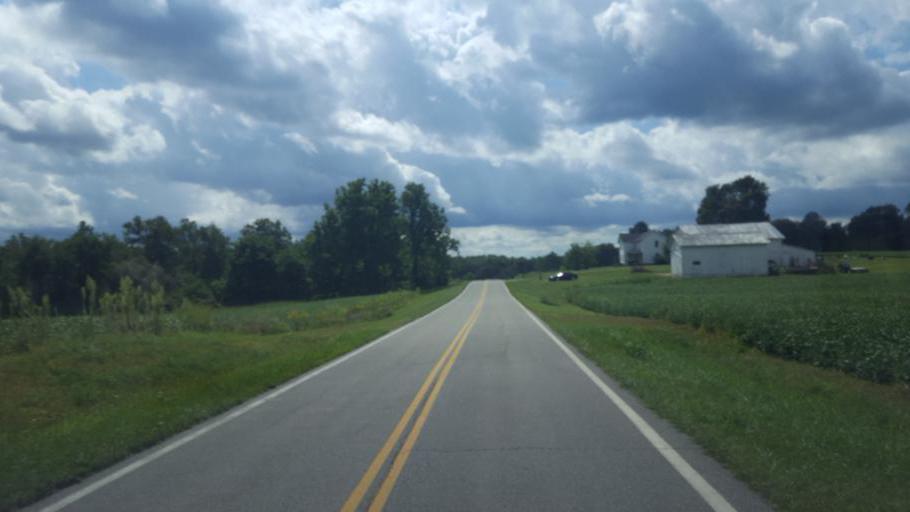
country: US
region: Ohio
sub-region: Huron County
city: Norwalk
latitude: 41.1638
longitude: -82.6321
